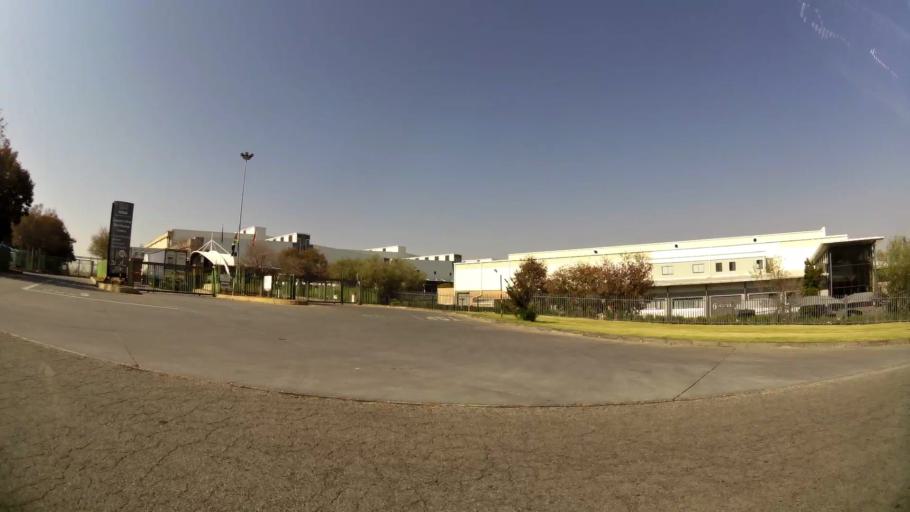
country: ZA
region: Gauteng
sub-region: City of Johannesburg Metropolitan Municipality
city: Modderfontein
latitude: -26.1084
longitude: 28.1328
